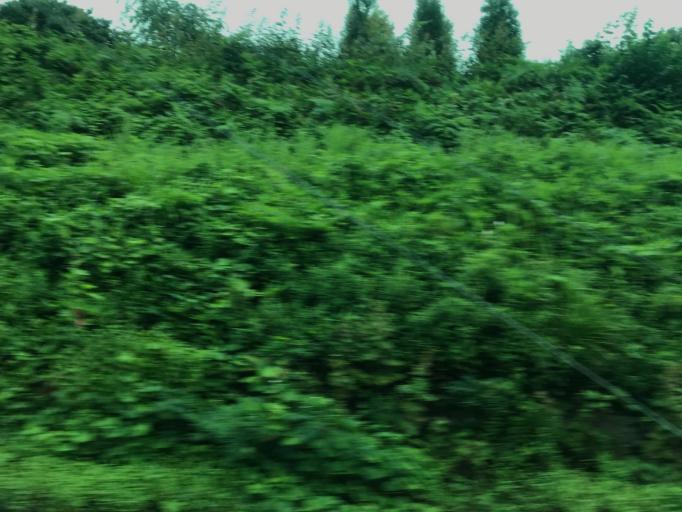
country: JP
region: Tochigi
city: Kuroiso
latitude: 37.0363
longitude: 140.1426
